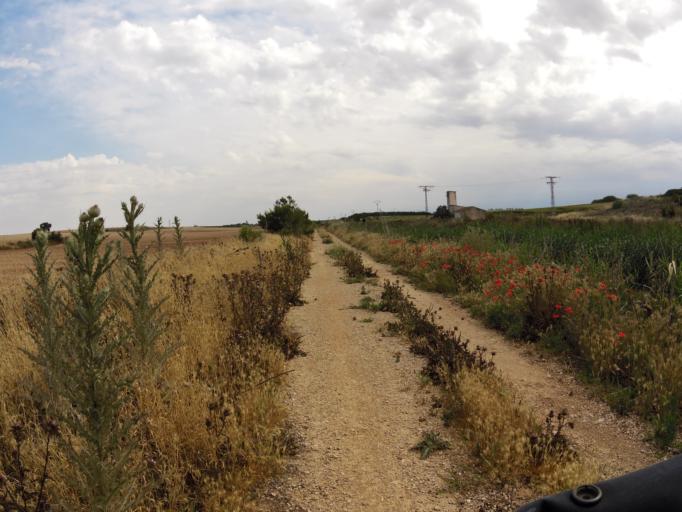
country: ES
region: Castille-La Mancha
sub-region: Provincia de Albacete
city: Albacete
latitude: 39.0482
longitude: -1.7606
